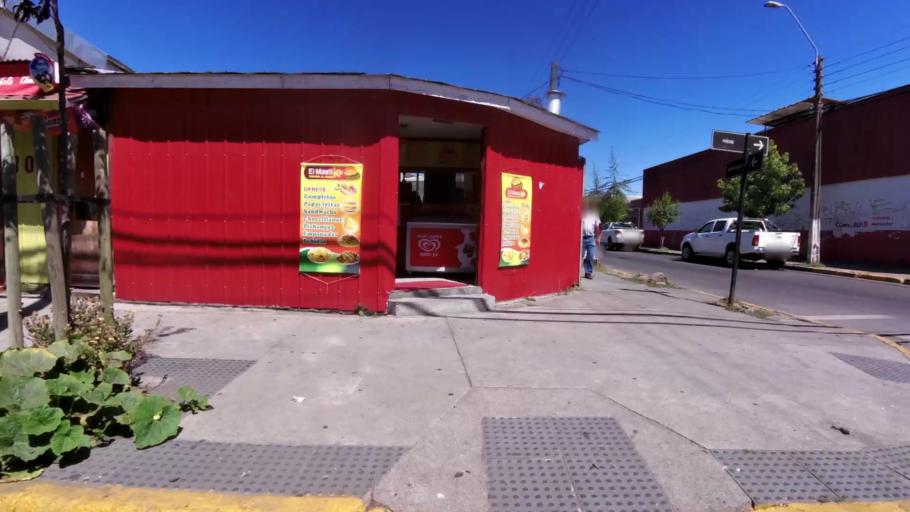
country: CL
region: Biobio
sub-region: Provincia de Concepcion
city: Penco
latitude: -36.7361
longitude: -72.9912
